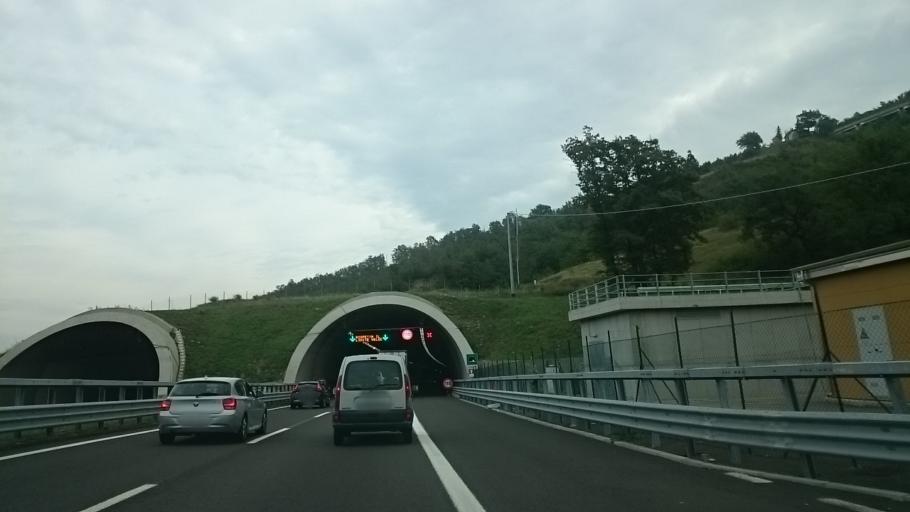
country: IT
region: Emilia-Romagna
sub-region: Provincia di Bologna
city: Grizzana
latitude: 44.2392
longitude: 11.1872
